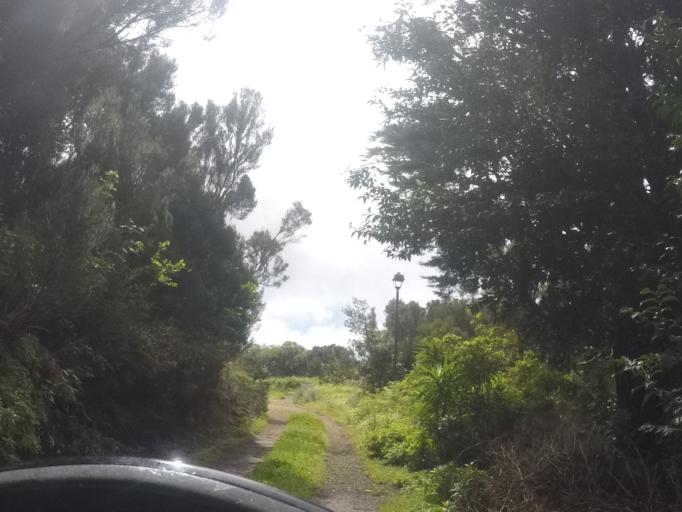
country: ES
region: Canary Islands
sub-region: Provincia de Santa Cruz de Tenerife
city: Santa Cruz de Tenerife
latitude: 28.5375
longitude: -16.2345
